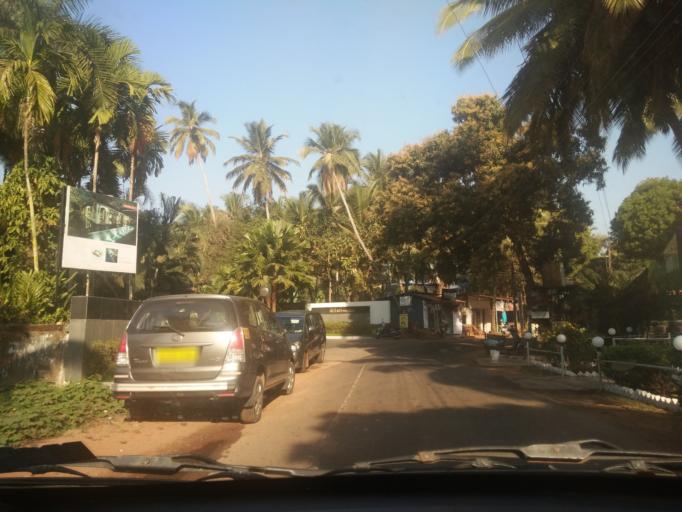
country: IN
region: Goa
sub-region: South Goa
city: Colva
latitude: 15.3062
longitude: 73.9124
